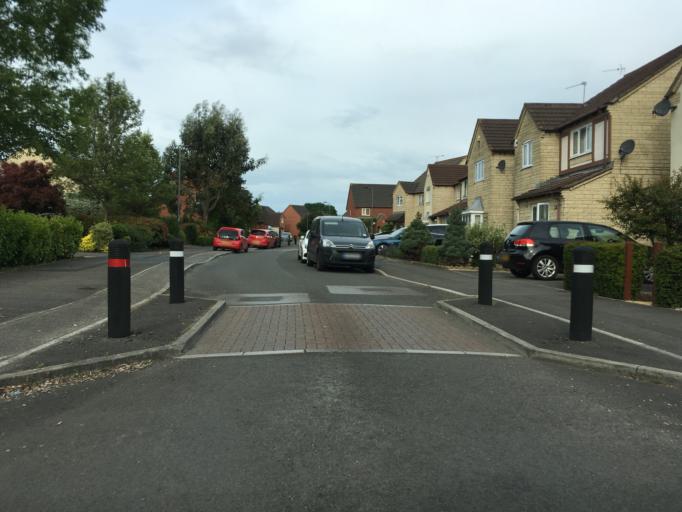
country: GB
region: England
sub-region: South Gloucestershire
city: Almondsbury
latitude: 51.5379
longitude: -2.5533
